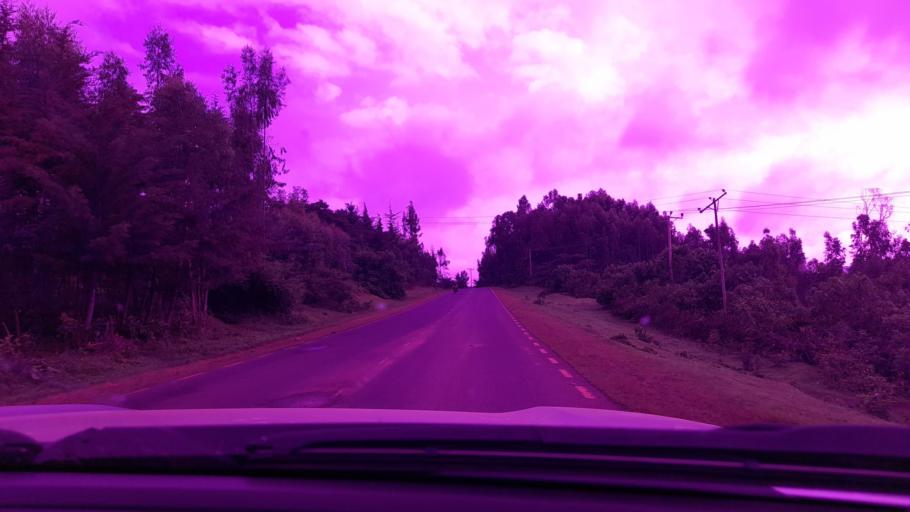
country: ET
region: Oromiya
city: Bedele
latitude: 8.2968
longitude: 36.4493
